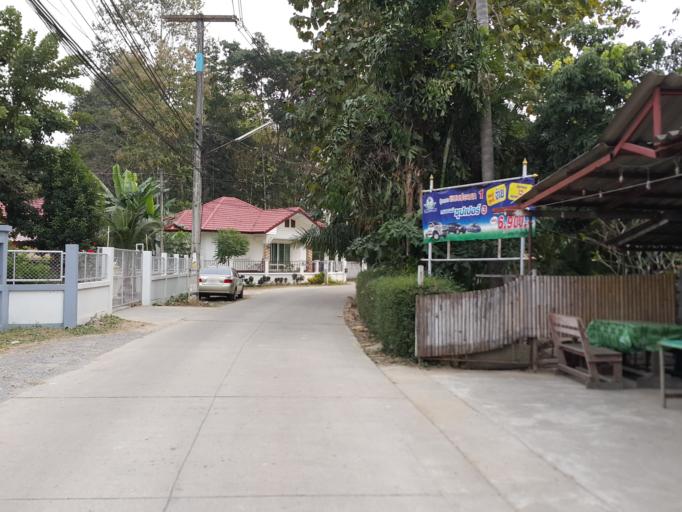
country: TH
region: Chiang Mai
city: Saraphi
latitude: 18.7395
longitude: 99.0186
